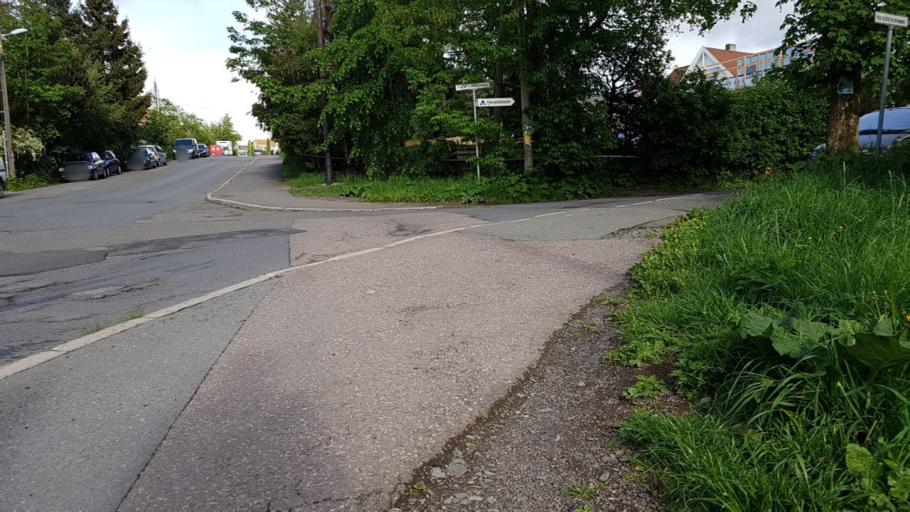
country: NO
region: Oslo
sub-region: Oslo
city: Oslo
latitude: 59.9437
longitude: 10.7878
